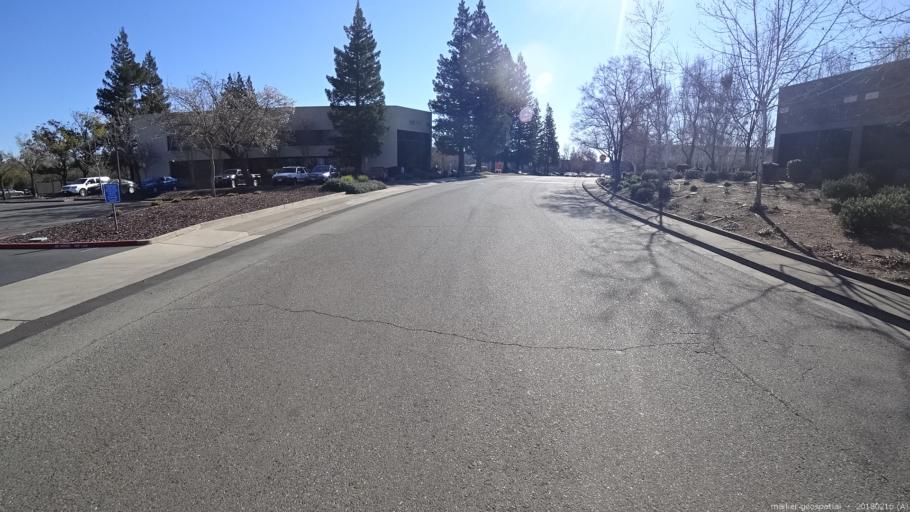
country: US
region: California
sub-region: Sacramento County
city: Gold River
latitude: 38.6232
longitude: -121.2626
